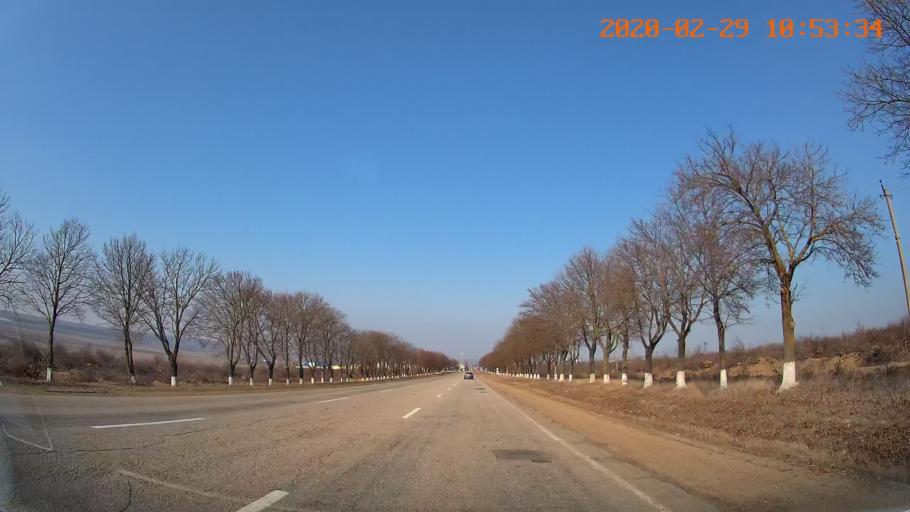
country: MD
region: Telenesti
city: Grigoriopol
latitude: 47.1170
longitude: 29.3337
